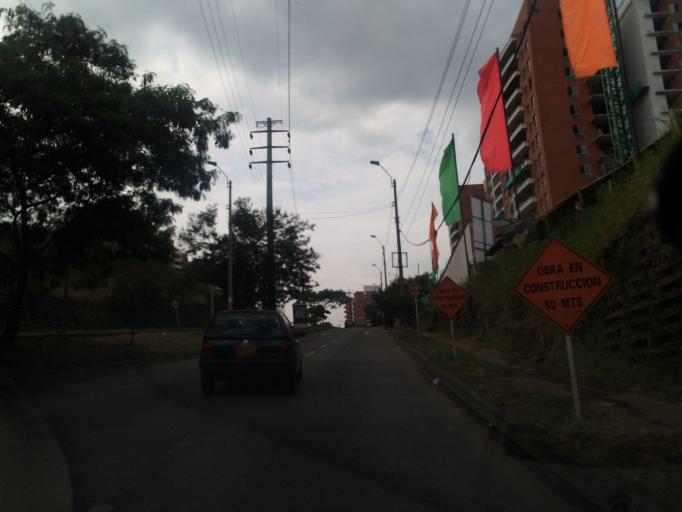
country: CO
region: Valle del Cauca
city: Cali
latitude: 3.4290
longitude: -76.5519
